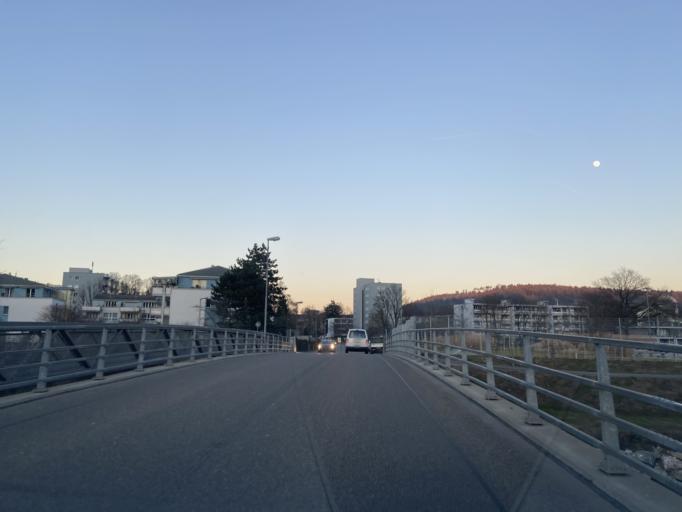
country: CH
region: Zurich
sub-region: Bezirk Winterthur
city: Wuelflingen (Kreis 6)
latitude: 47.5118
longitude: 8.6826
